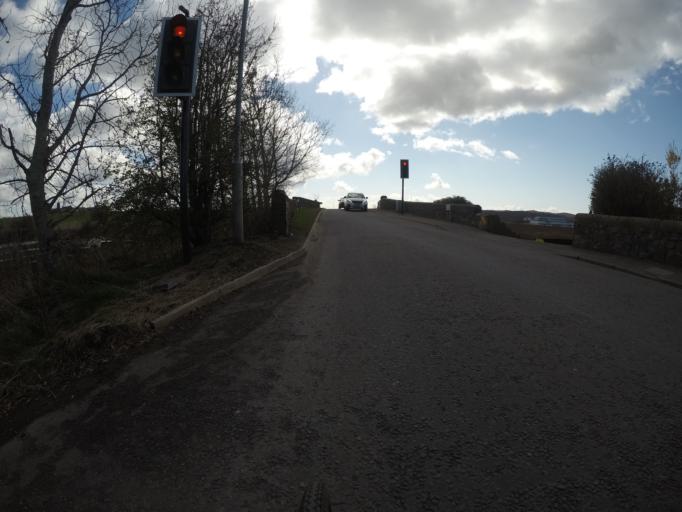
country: GB
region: Scotland
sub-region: North Ayrshire
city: Dreghorn
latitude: 55.5945
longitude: -4.6039
